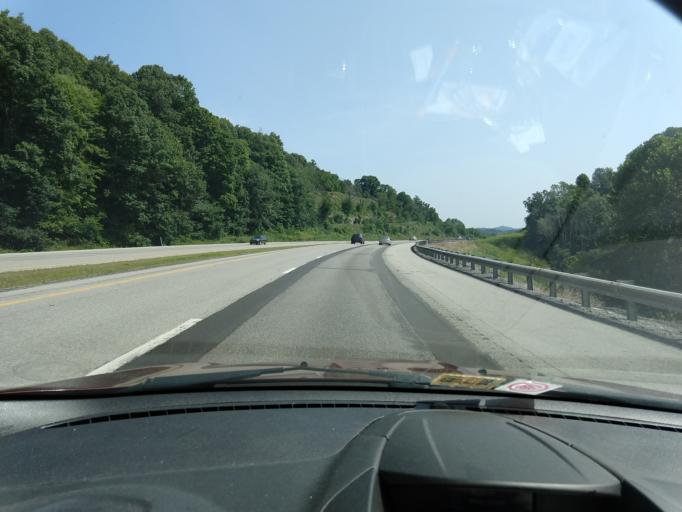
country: US
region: West Virginia
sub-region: Lewis County
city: Weston
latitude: 38.9080
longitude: -80.6025
